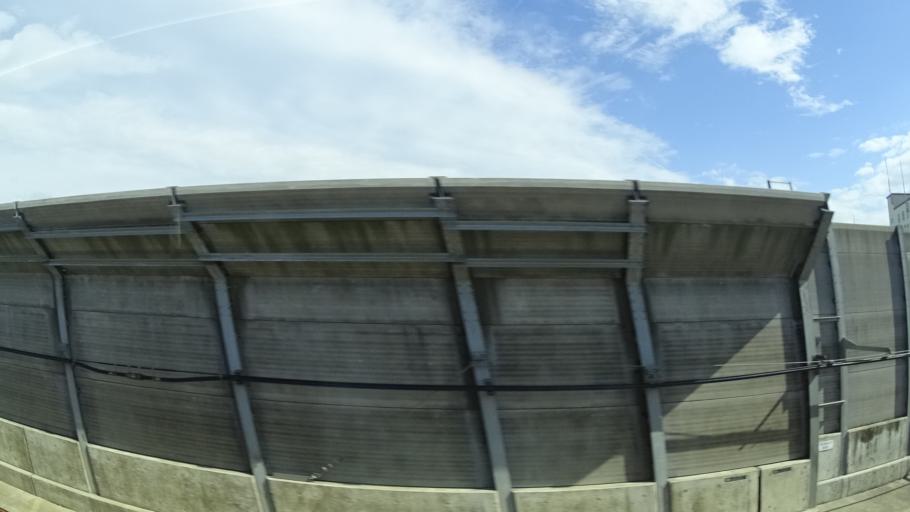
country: JP
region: Toyama
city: Takaoka
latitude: 36.7177
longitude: 136.9724
